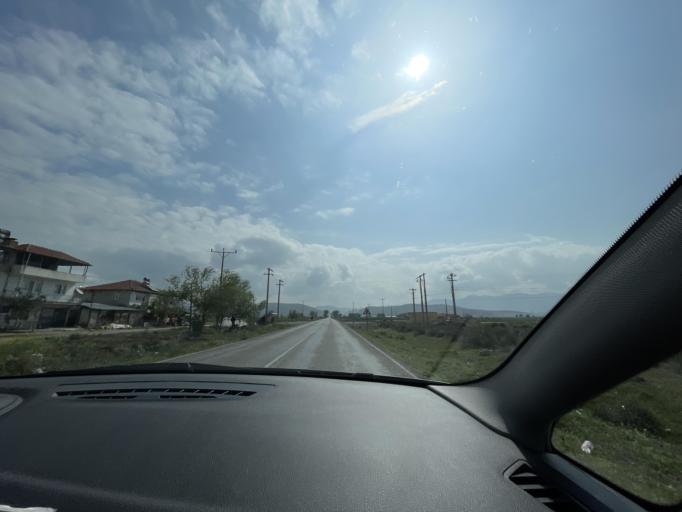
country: TR
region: Denizli
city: Acipayam
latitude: 37.5084
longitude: 29.4073
